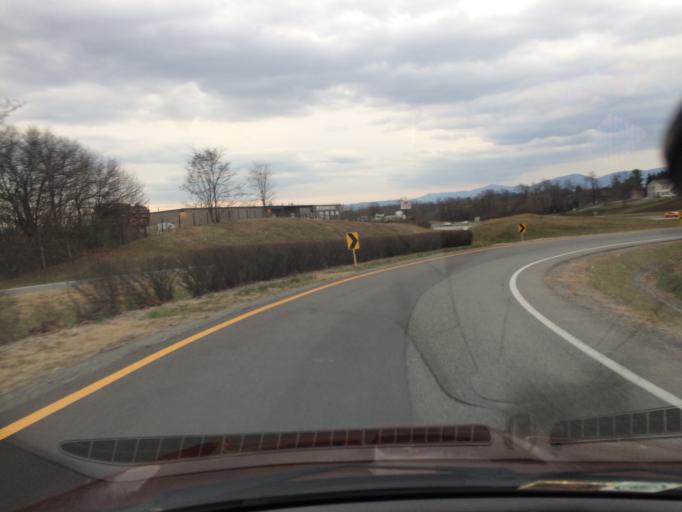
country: US
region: Virginia
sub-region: Roanoke County
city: Hollins
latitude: 37.3273
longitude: -79.9868
